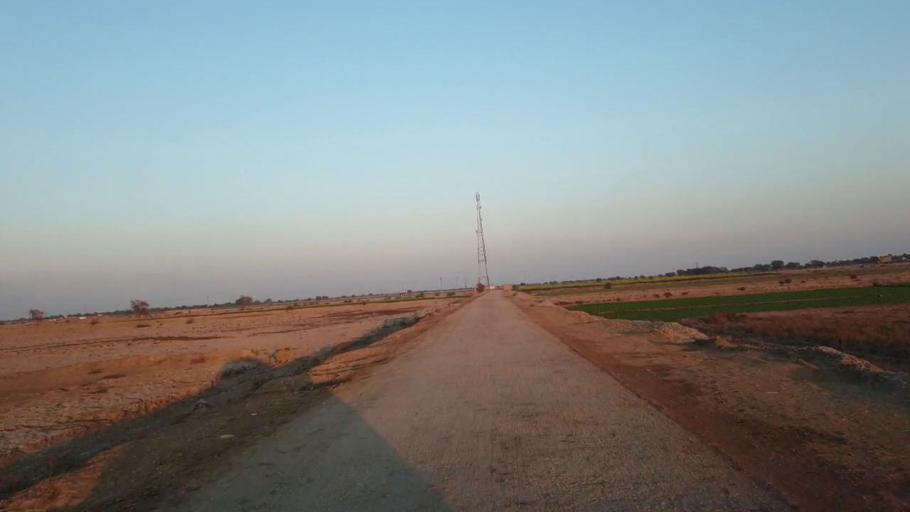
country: PK
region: Sindh
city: Shahpur Chakar
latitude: 26.1685
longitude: 68.5543
